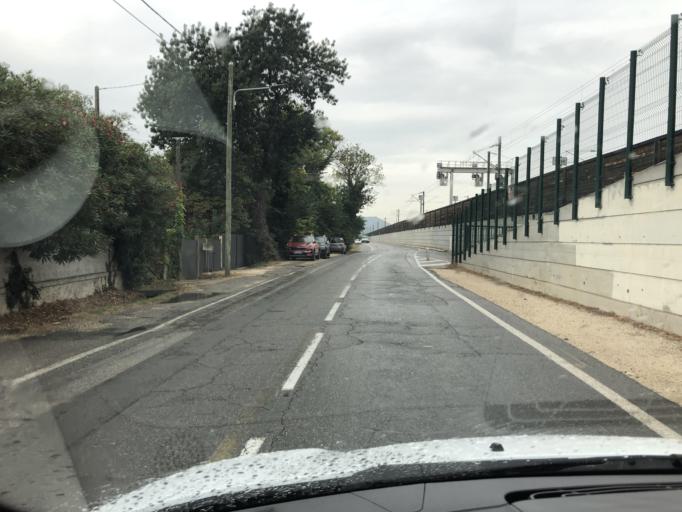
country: FR
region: Provence-Alpes-Cote d'Azur
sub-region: Departement des Bouches-du-Rhone
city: Aubagne
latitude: 43.2872
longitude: 5.5438
